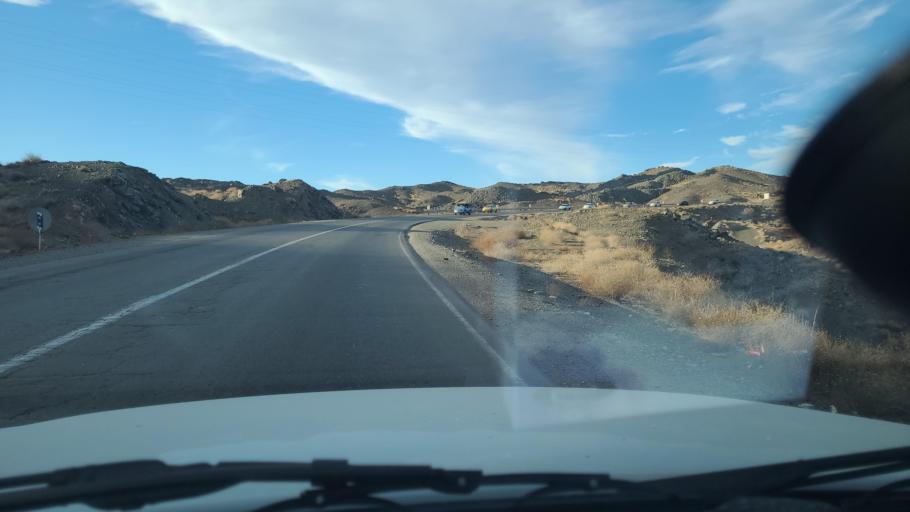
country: IR
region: Razavi Khorasan
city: Sabzevar
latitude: 36.4024
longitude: 57.5490
